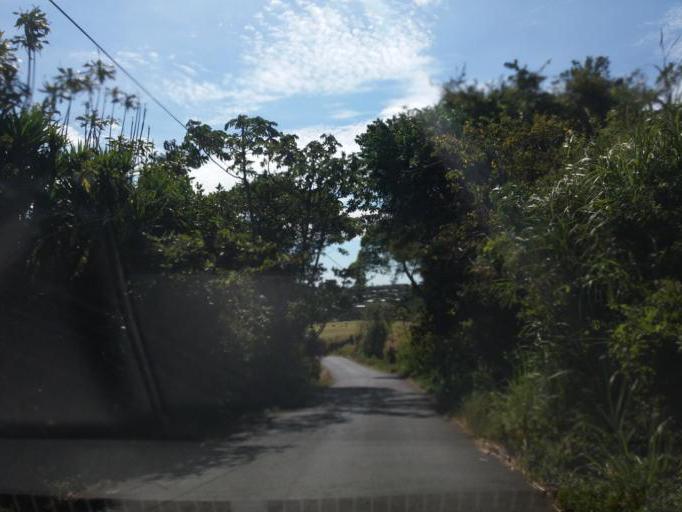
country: CR
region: Heredia
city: Santo Domingo
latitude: 10.0500
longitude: -84.1552
